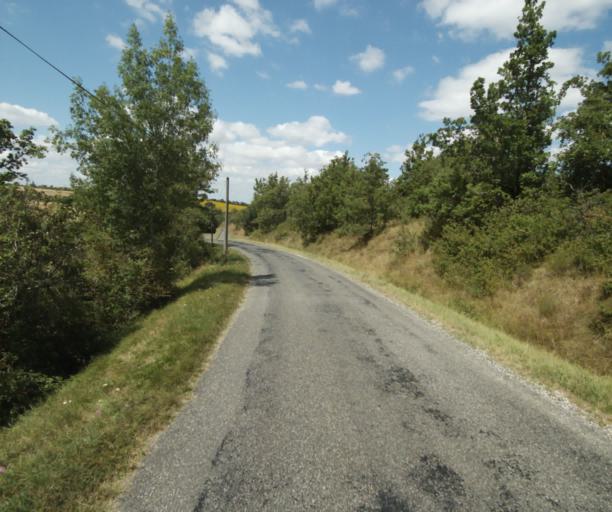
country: FR
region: Midi-Pyrenees
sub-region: Departement de la Haute-Garonne
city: Saint-Felix-Lauragais
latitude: 43.4669
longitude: 1.8550
